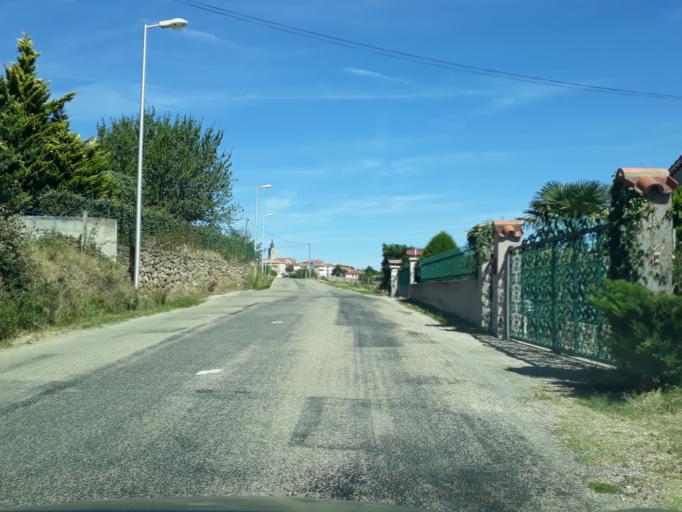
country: FR
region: Rhone-Alpes
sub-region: Departement de l'Ardeche
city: Felines
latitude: 45.3110
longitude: 4.7276
